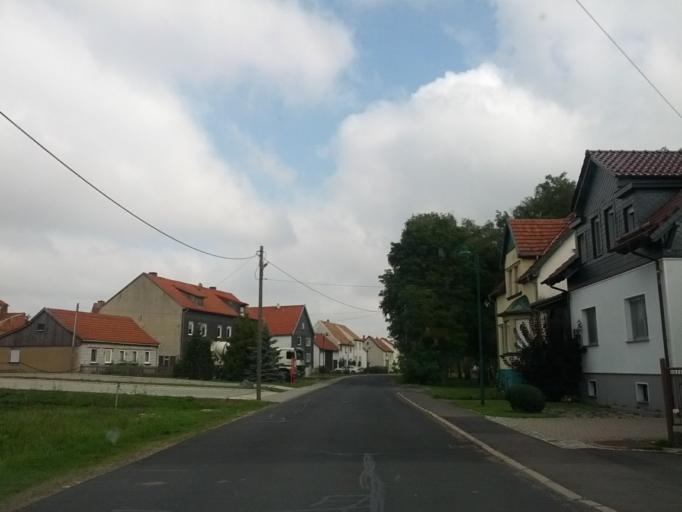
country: DE
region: Thuringia
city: Ernstroda
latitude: 50.8998
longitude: 10.6253
